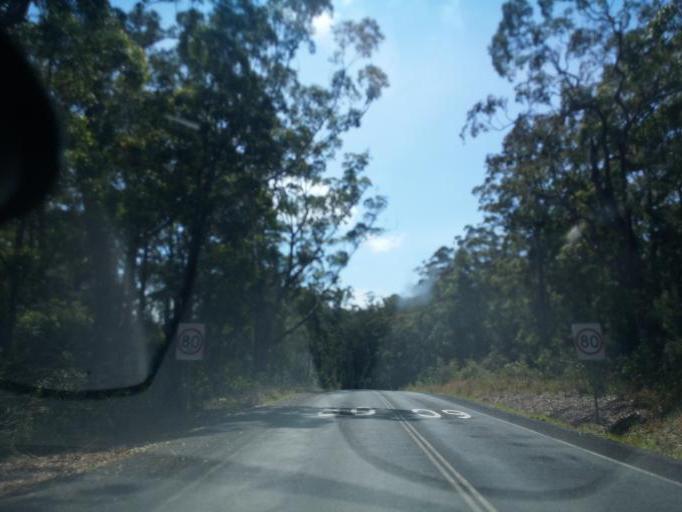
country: AU
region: New South Wales
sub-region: Great Lakes
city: Forster
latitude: -32.3830
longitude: 152.4475
